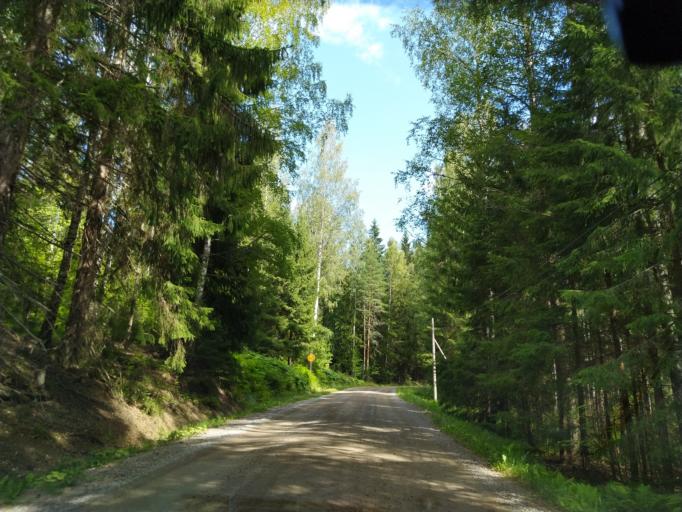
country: FI
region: Pirkanmaa
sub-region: Ylae-Pirkanmaa
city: Ruovesi
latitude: 61.9578
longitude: 24.0246
